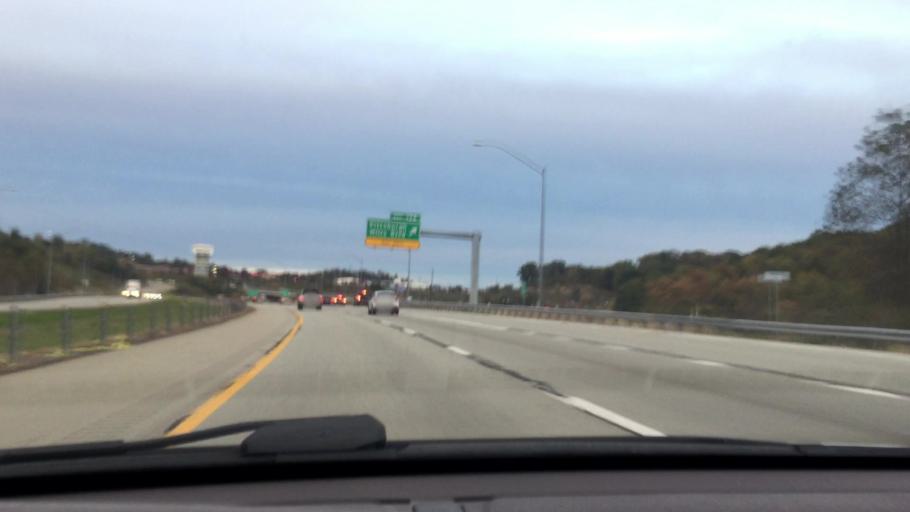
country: US
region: Pennsylvania
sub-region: Allegheny County
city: Cheswick
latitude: 40.5622
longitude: -79.7999
